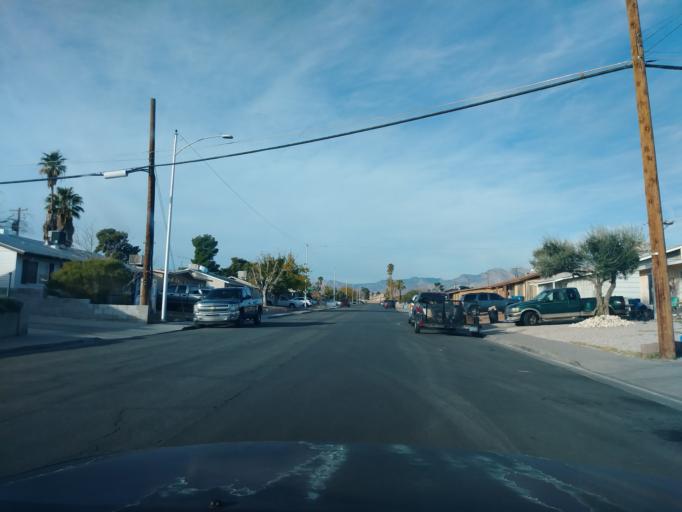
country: US
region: Nevada
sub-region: Clark County
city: Spring Valley
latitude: 36.1657
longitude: -115.2366
